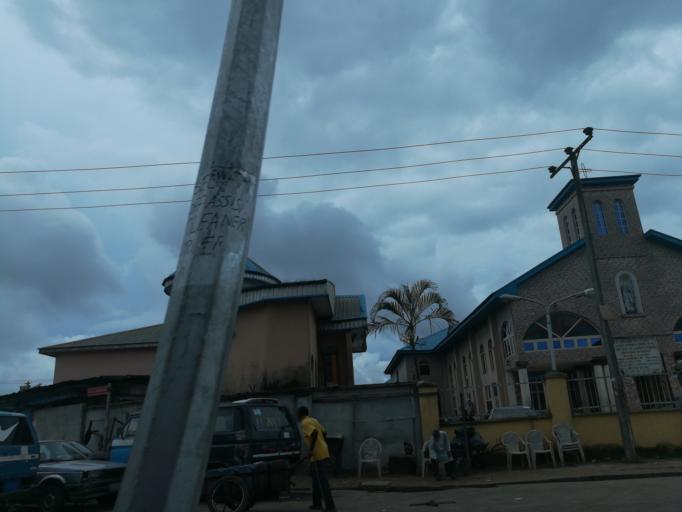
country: NG
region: Rivers
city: Port Harcourt
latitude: 4.7591
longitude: 7.0315
